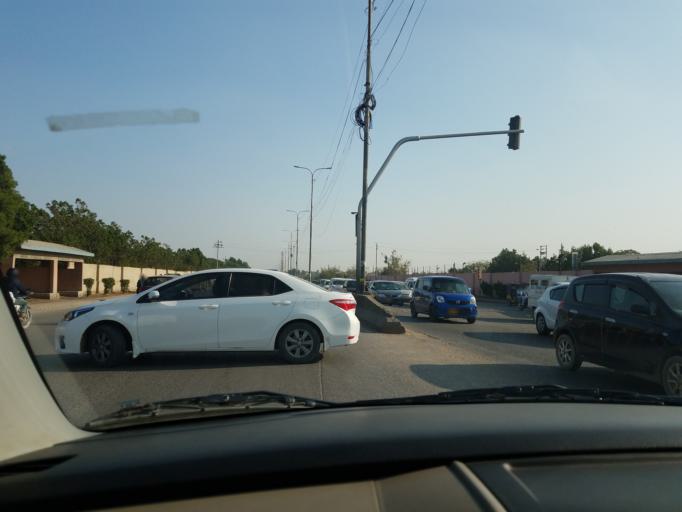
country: PK
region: Sindh
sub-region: Karachi District
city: Karachi
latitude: 24.8921
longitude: 67.1218
